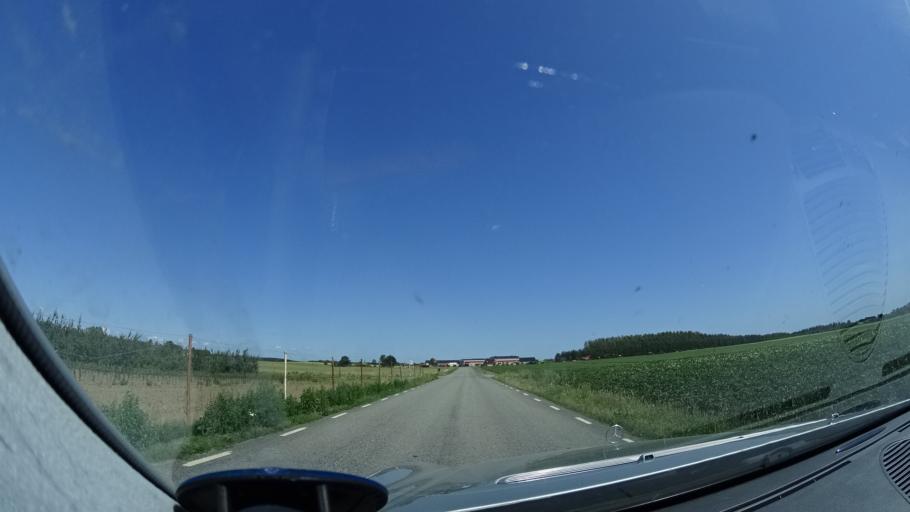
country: SE
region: Skane
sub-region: Kristianstads Kommun
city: Degeberga
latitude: 55.8899
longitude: 14.0357
